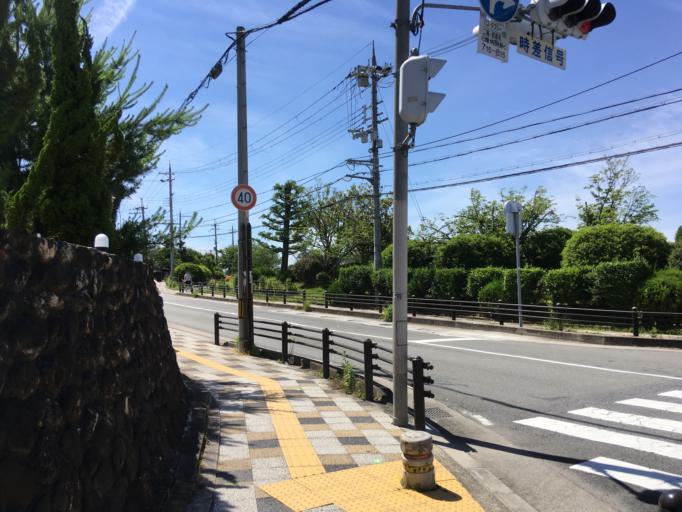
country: JP
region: Nara
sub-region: Ikoma-shi
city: Ikoma
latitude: 34.7083
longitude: 135.7501
